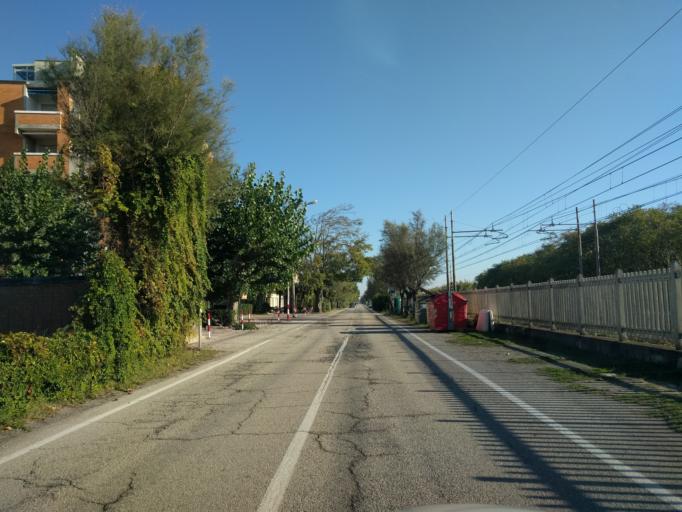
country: IT
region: The Marches
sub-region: Provincia di Pesaro e Urbino
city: Marotta
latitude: 43.7969
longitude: 13.0975
